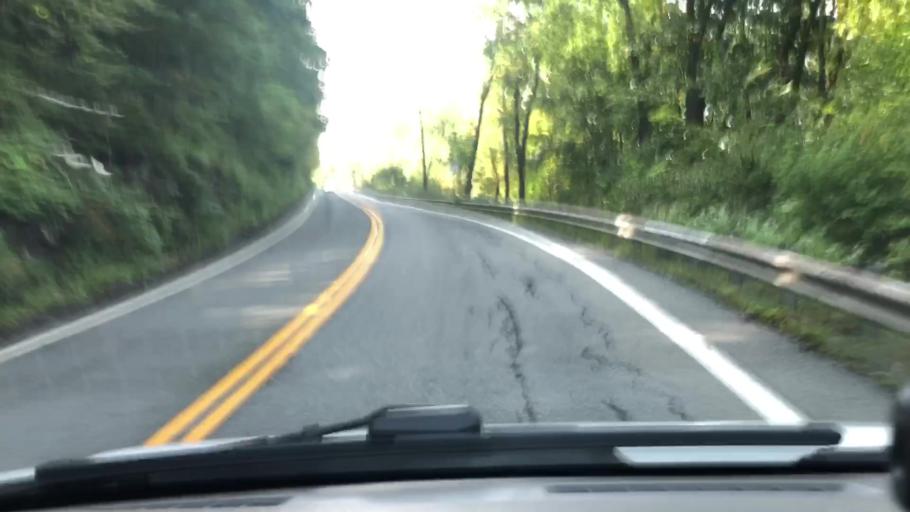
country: US
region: Massachusetts
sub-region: Berkshire County
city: North Adams
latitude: 42.7049
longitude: -73.0644
